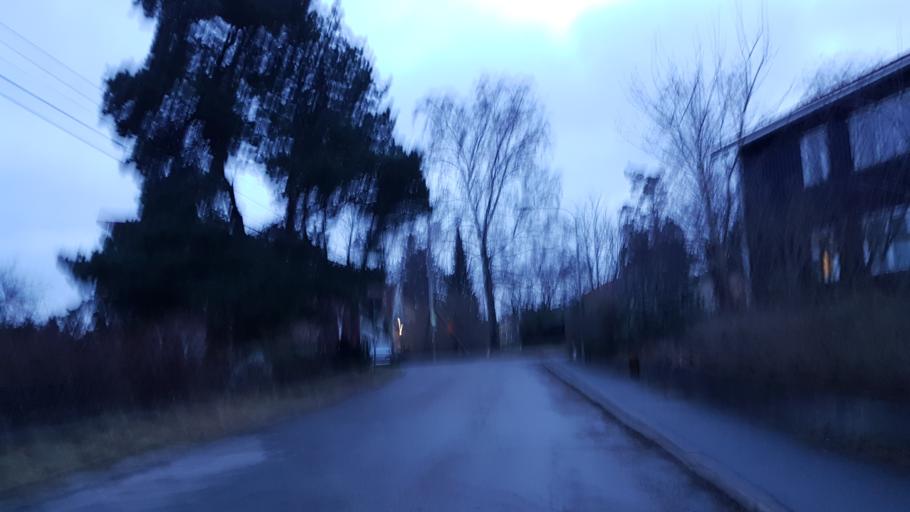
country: SE
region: Stockholm
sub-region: Stockholms Kommun
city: Arsta
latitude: 59.2777
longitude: 18.0511
